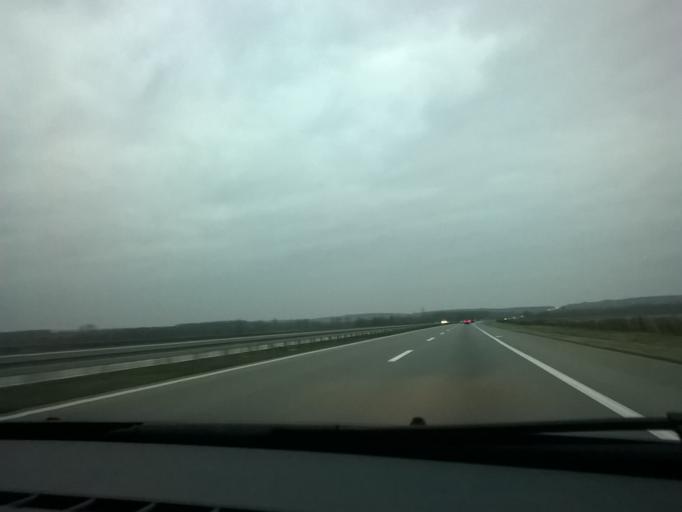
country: RS
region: Autonomna Pokrajina Vojvodina
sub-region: Juznobacki Okrug
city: Kovilj
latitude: 45.2024
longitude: 20.0719
